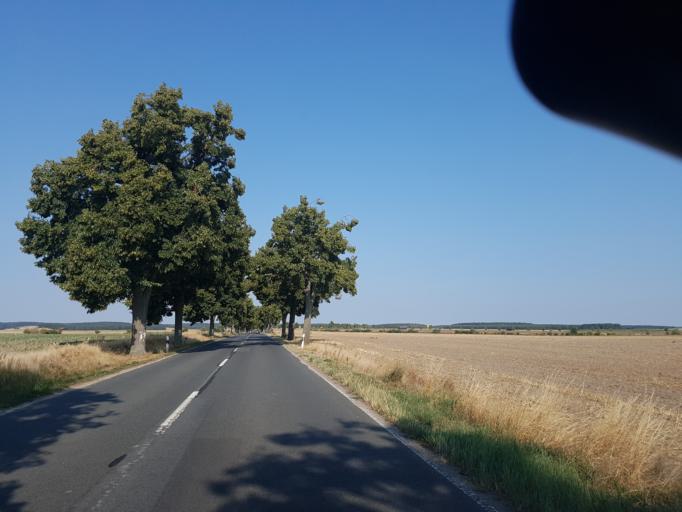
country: DE
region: Brandenburg
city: Niemegk
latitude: 52.1032
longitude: 12.6608
